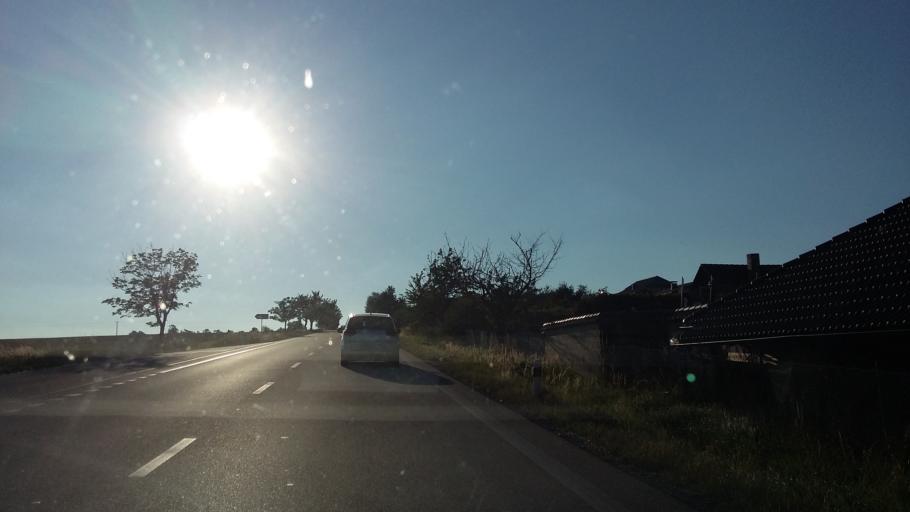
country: CZ
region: Vysocina
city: Velky Beranov
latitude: 49.4023
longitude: 15.6661
